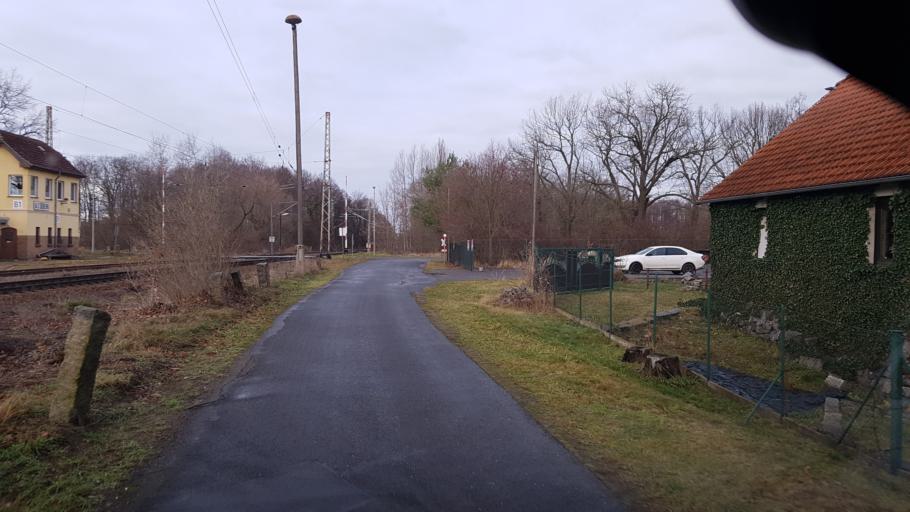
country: DE
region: Brandenburg
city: Altdobern
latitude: 51.6566
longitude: 14.0080
